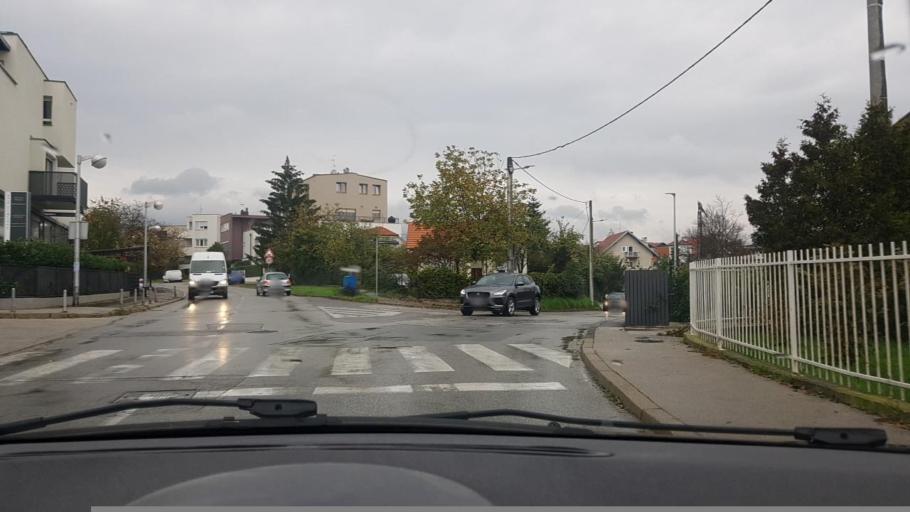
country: HR
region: Grad Zagreb
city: Zagreb
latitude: 45.8289
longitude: 15.9958
